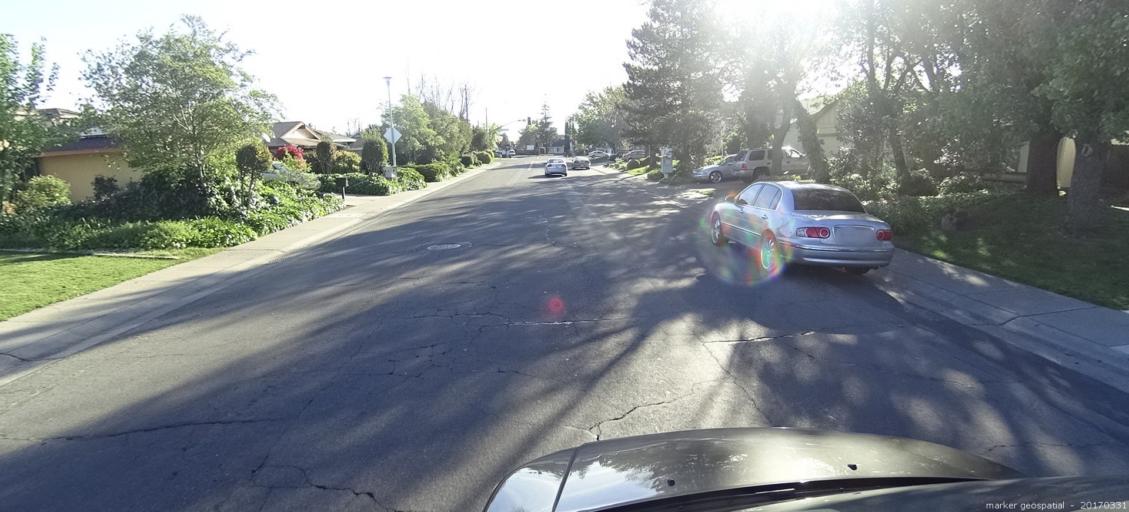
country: US
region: California
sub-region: Sacramento County
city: Parkway
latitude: 38.4707
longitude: -121.4504
